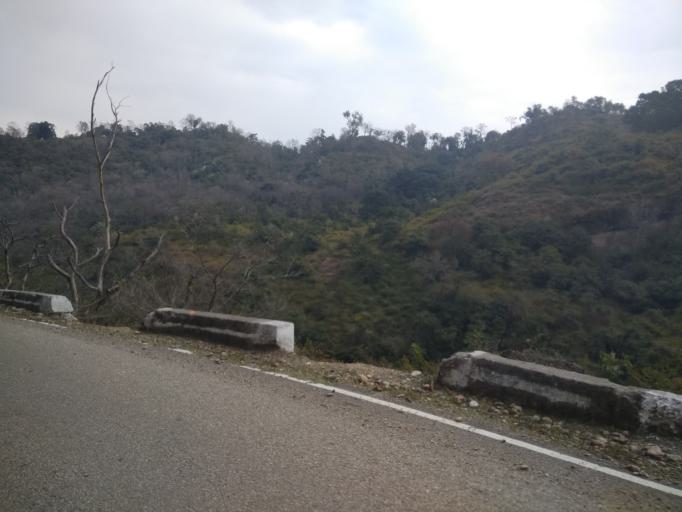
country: IN
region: Himachal Pradesh
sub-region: Kangra
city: Kotla
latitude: 32.2261
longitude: 76.0626
